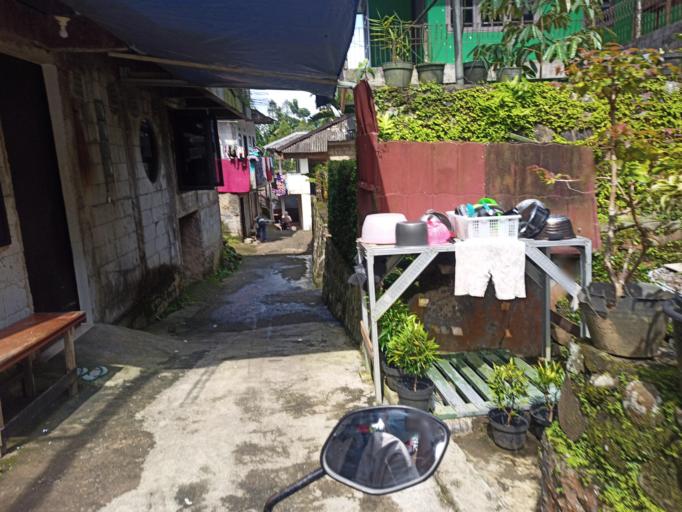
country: ID
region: West Java
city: Caringin
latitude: -6.6428
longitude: 106.9140
